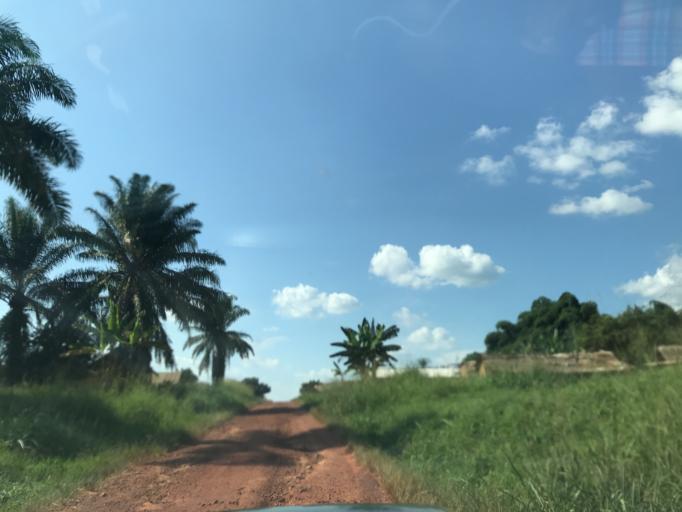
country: CD
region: Eastern Province
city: Kisangani
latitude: 1.3902
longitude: 25.2596
